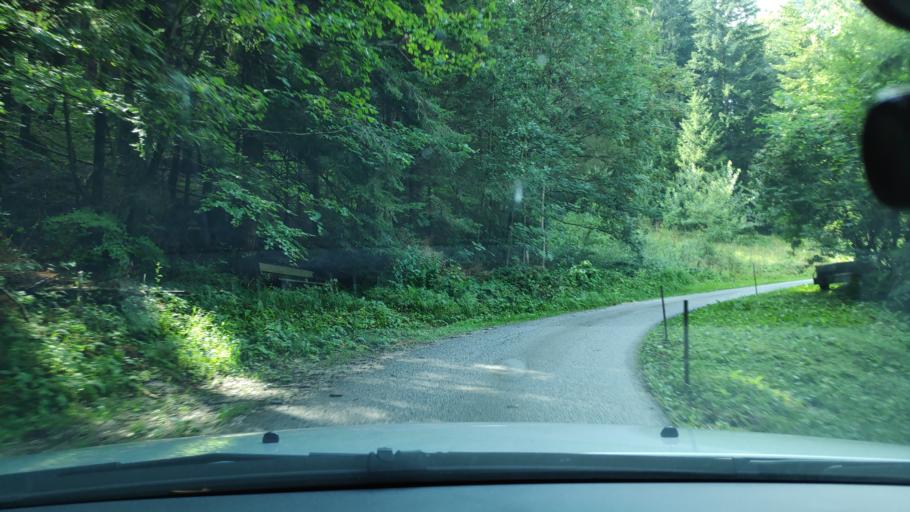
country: AT
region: Lower Austria
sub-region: Politischer Bezirk Wiener Neustadt
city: Miesenbach
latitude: 47.8319
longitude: 15.9687
